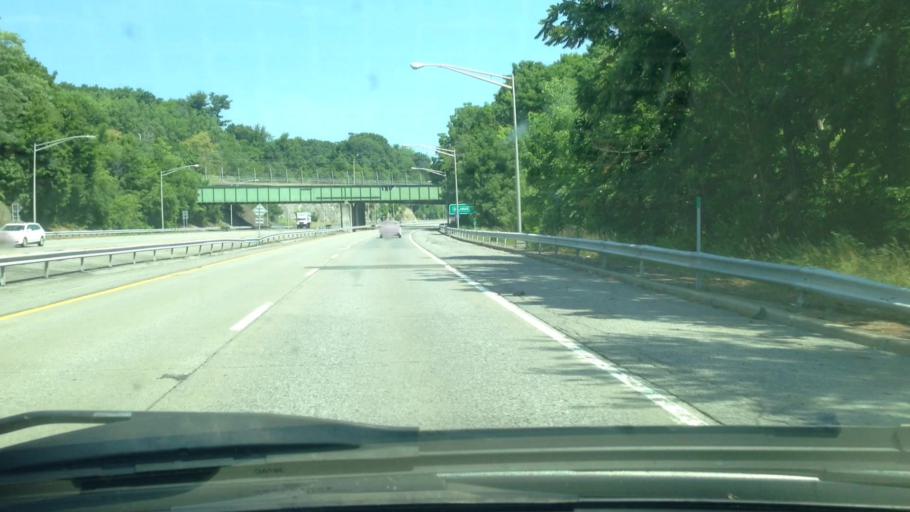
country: US
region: New York
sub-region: Ulster County
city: Kingston
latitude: 41.9249
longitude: -73.9855
